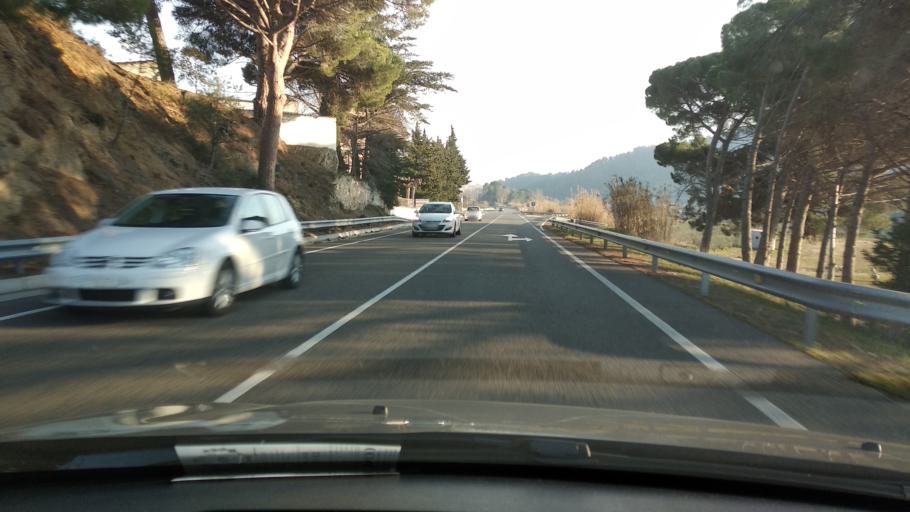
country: ES
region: Catalonia
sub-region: Provincia de Tarragona
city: Alforja
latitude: 41.1934
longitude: 0.9990
